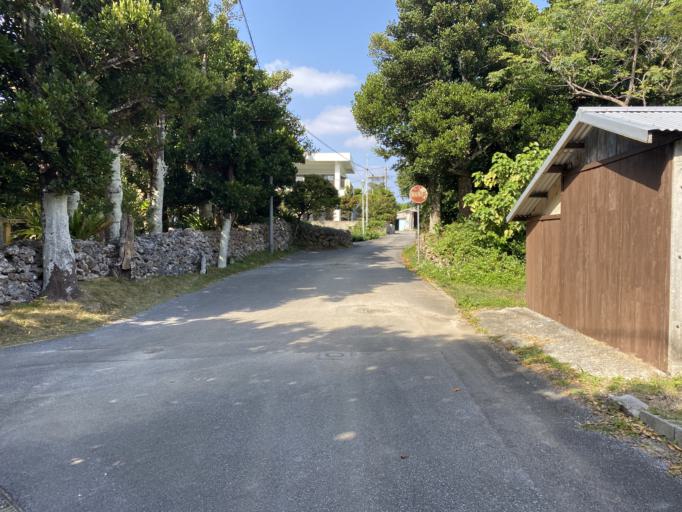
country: JP
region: Okinawa
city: Ishigaki
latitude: 24.0603
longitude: 123.7771
